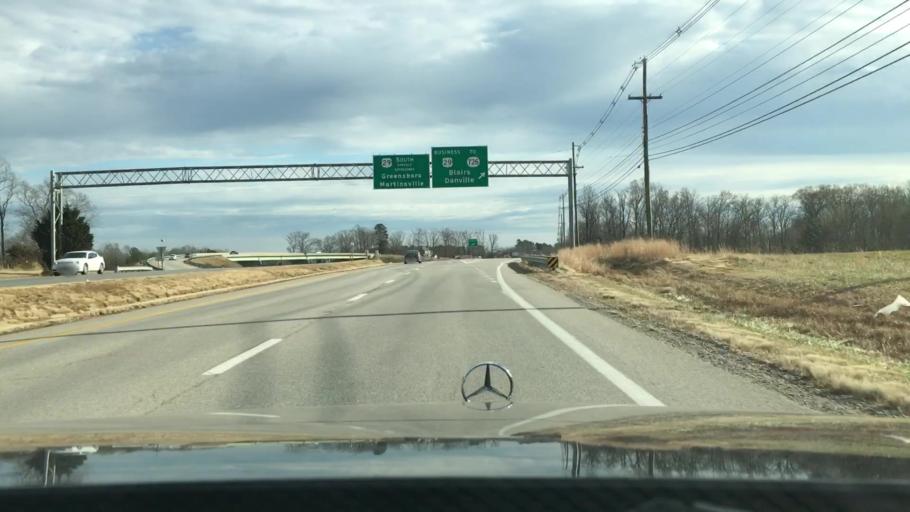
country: US
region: Virginia
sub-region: Pittsylvania County
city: Mount Hermon
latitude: 36.7045
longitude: -79.3713
